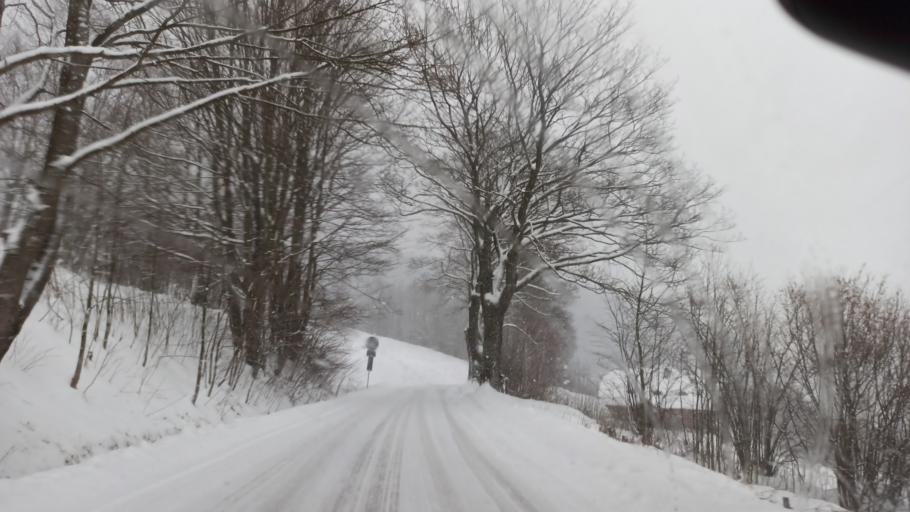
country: PL
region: Lower Silesian Voivodeship
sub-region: Powiat klodzki
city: Ludwikowice Klodzkie
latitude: 50.6601
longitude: 16.4712
